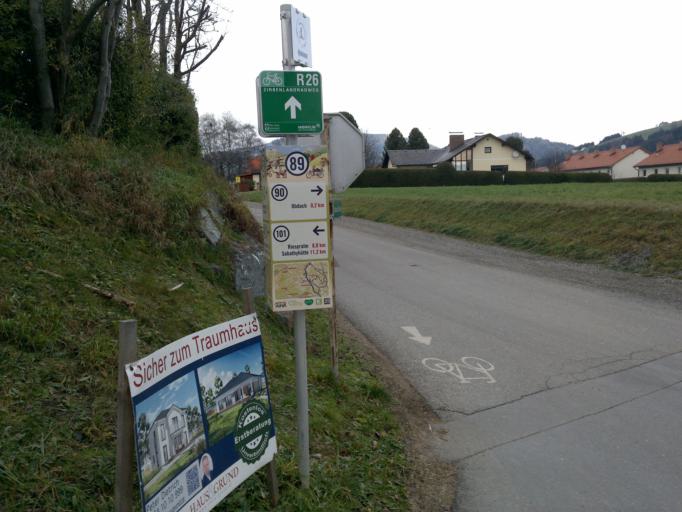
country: AT
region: Styria
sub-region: Politischer Bezirk Murtal
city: Obdach
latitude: 47.0688
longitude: 14.6921
